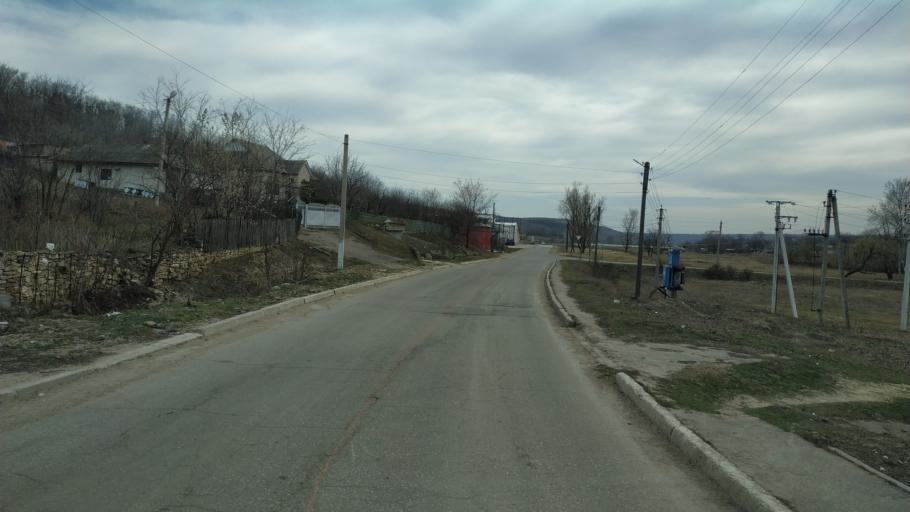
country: MD
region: Nisporeni
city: Nisporeni
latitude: 46.9634
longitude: 28.2162
